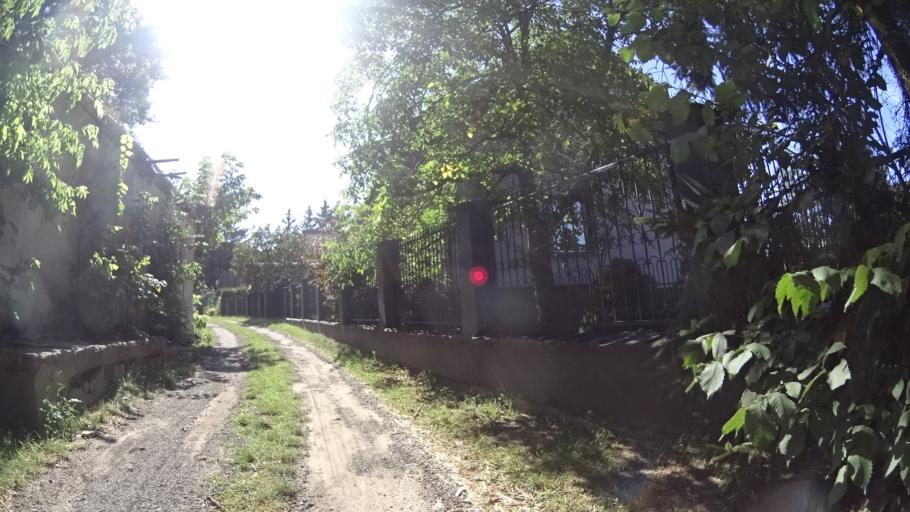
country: PL
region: Masovian Voivodeship
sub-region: Powiat bialobrzeski
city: Promna
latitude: 51.6733
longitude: 20.9421
